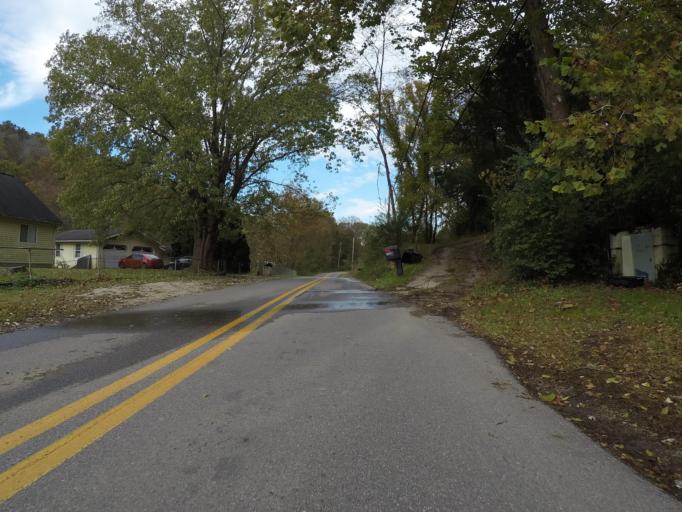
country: US
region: West Virginia
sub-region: Wayne County
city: Lavalette
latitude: 38.3401
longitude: -82.4497
